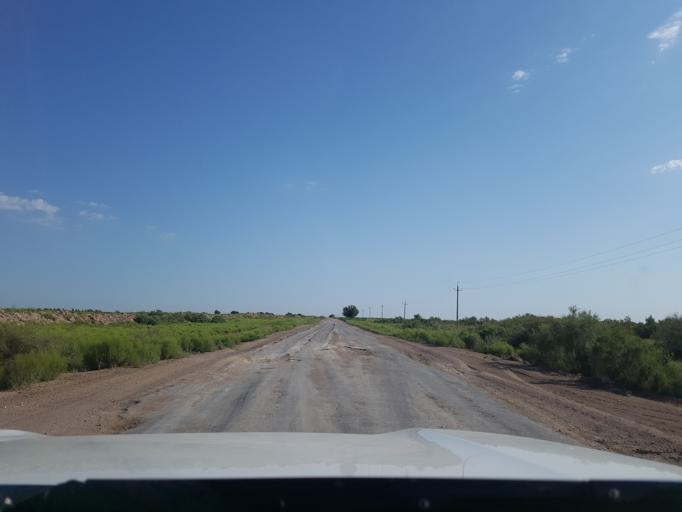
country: TM
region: Dasoguz
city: Koeneuergench
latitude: 41.9190
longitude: 58.7113
